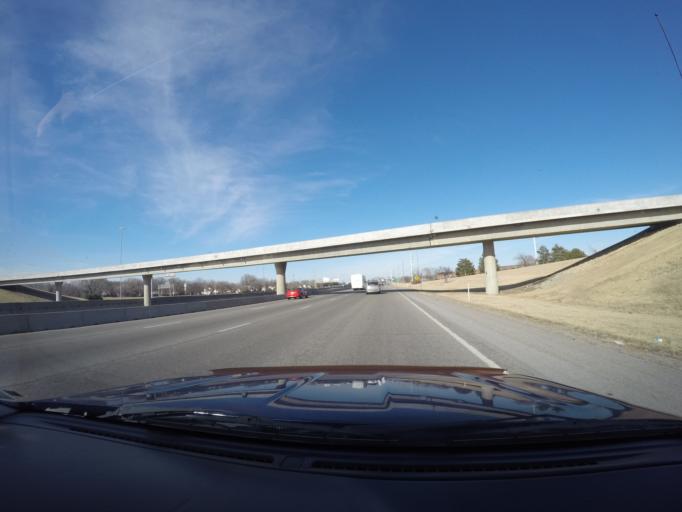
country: US
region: Kansas
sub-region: Sedgwick County
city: Wichita
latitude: 37.6800
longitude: -97.3123
